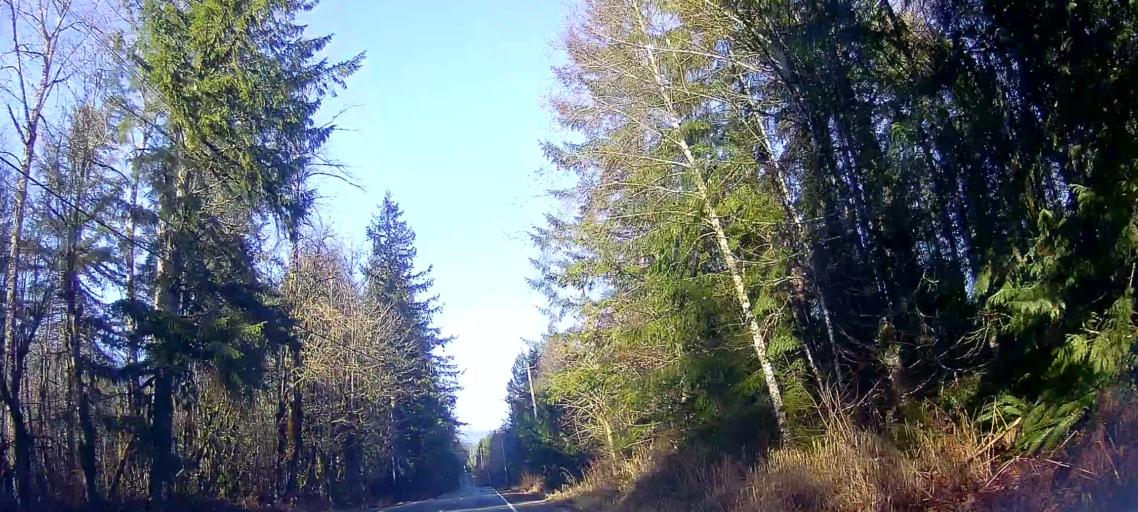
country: US
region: Washington
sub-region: Snohomish County
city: Darrington
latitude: 48.5579
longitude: -121.7658
